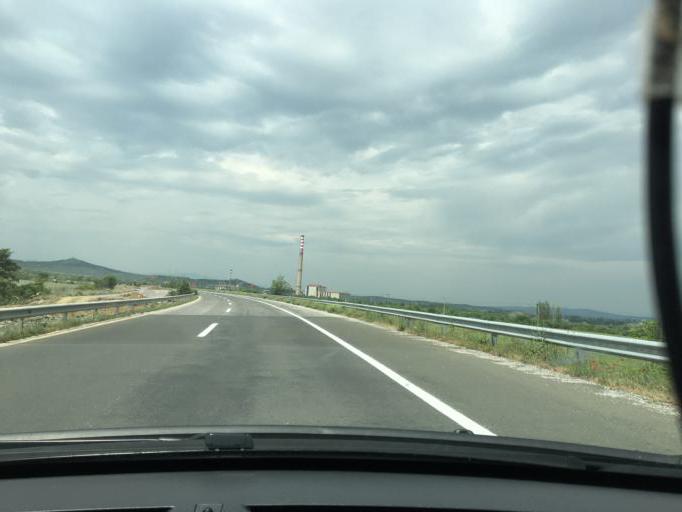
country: MK
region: Demir Kapija
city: Demir Kapija
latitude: 41.4503
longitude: 22.1747
